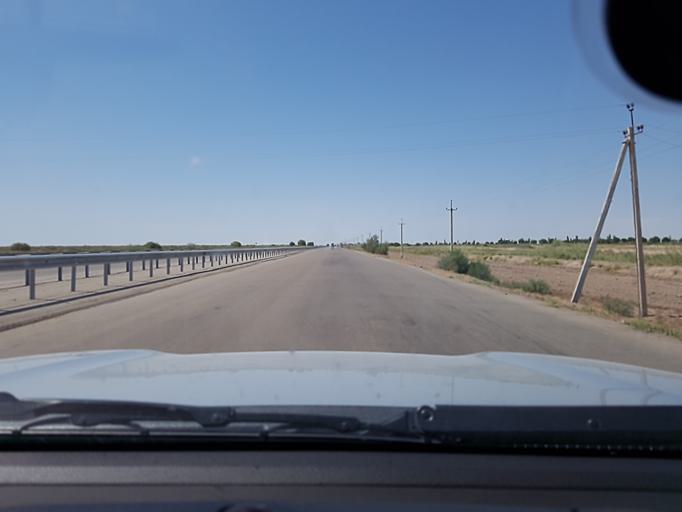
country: TM
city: Akdepe
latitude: 41.7384
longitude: 59.1711
